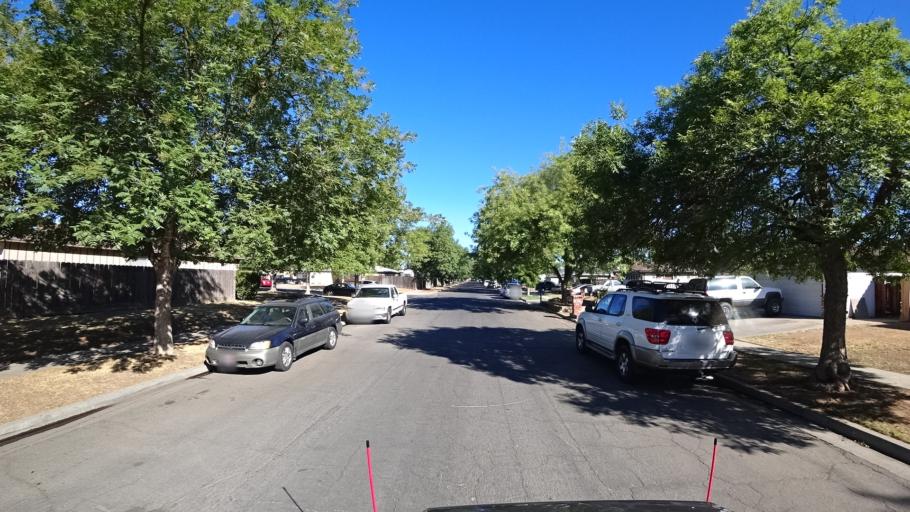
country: US
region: California
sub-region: Fresno County
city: Fresno
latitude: 36.8016
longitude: -119.8321
